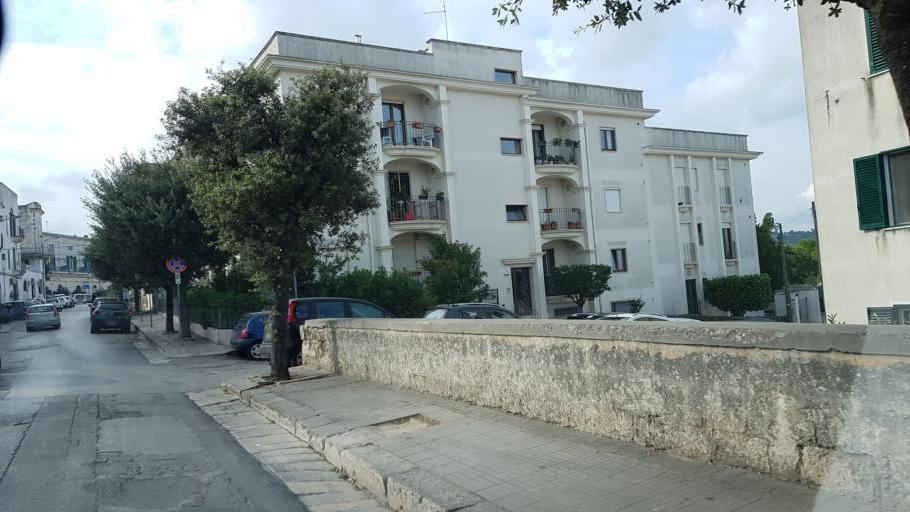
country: IT
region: Apulia
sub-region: Provincia di Brindisi
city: Ostuni
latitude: 40.7329
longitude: 17.5759
